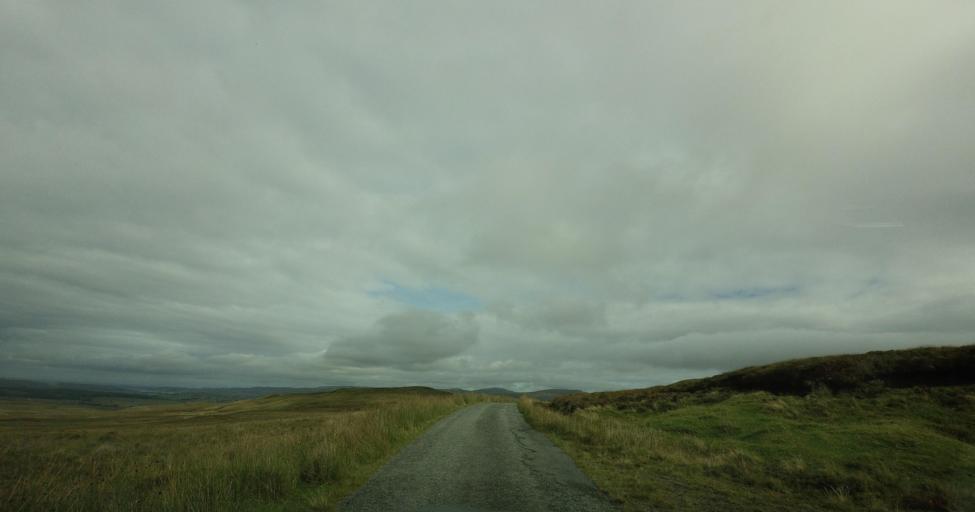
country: GB
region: Scotland
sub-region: Highland
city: Isle of Skye
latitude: 57.4060
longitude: -6.2663
